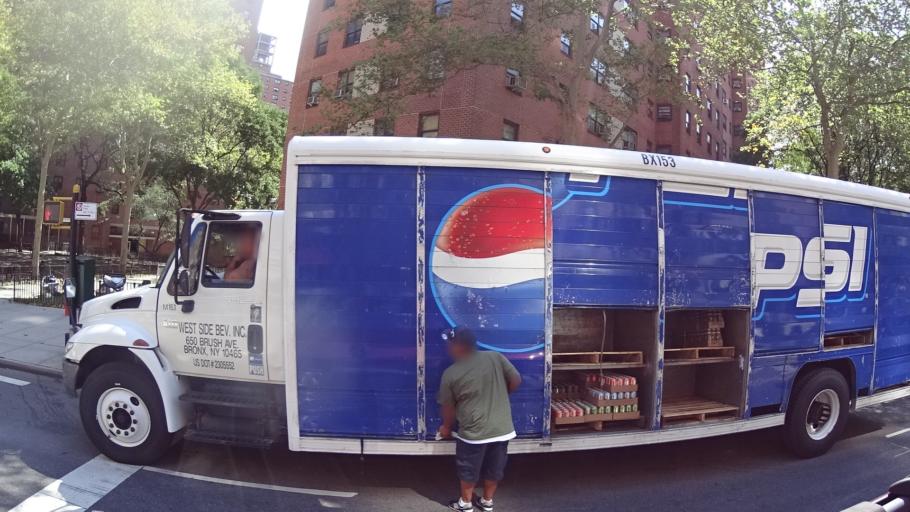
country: US
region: New Jersey
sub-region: Bergen County
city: Edgewater
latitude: 40.8118
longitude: -73.9574
